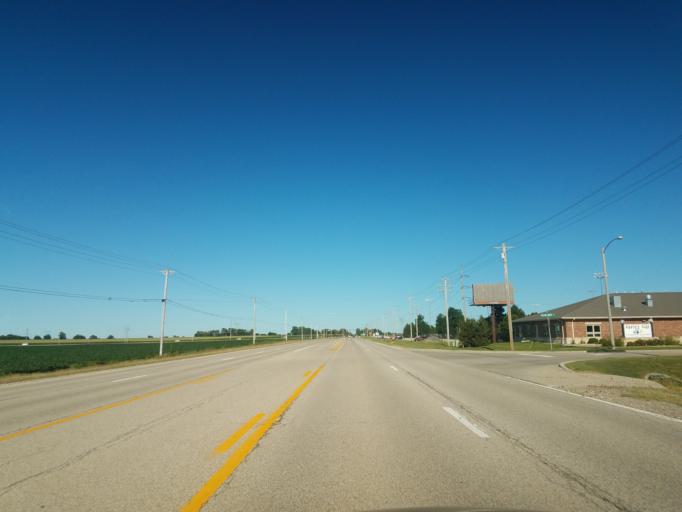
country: US
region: Illinois
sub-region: McLean County
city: Downs
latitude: 40.4583
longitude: -88.9078
